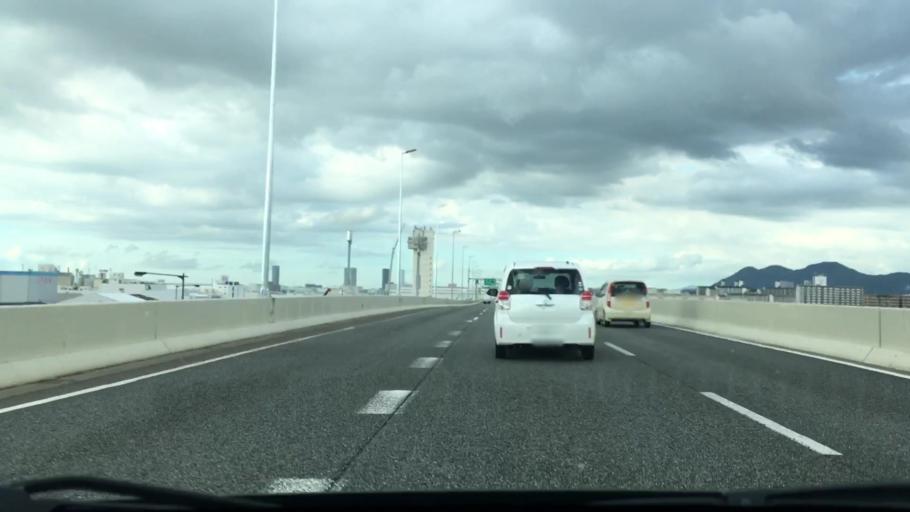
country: JP
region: Fukuoka
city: Fukuoka-shi
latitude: 33.6179
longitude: 130.4120
